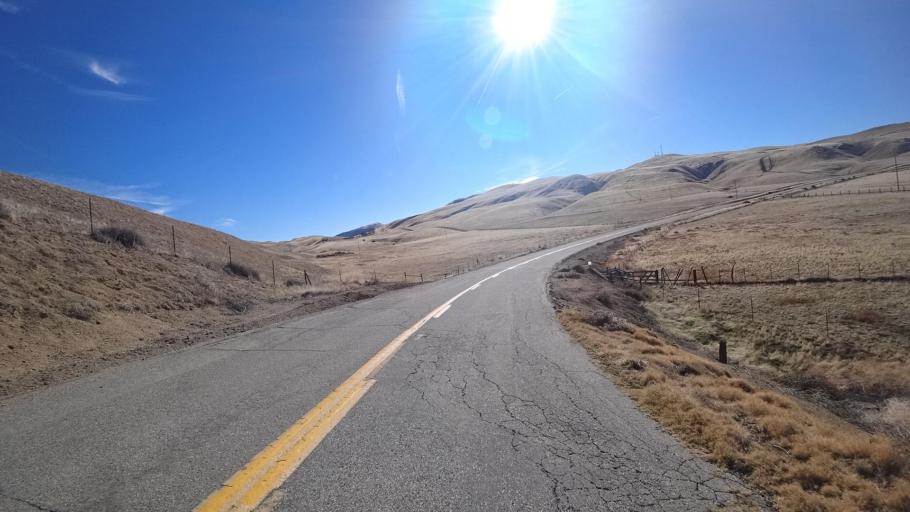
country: US
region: California
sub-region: Kern County
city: Maricopa
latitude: 34.9364
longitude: -119.4028
